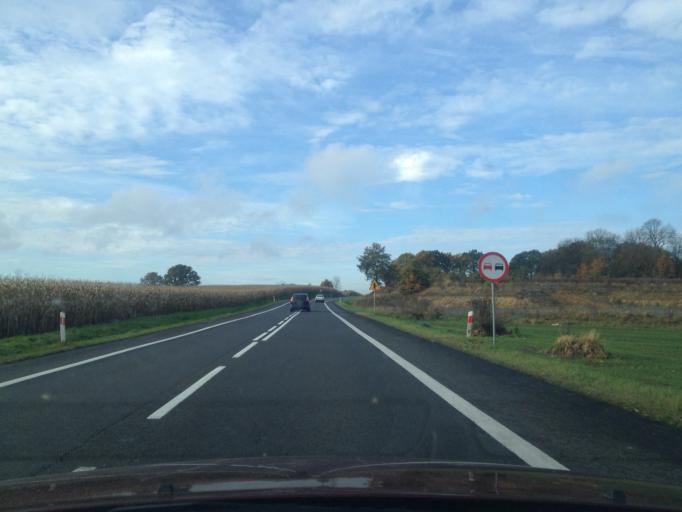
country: PL
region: Lower Silesian Voivodeship
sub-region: Powiat lubanski
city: Pisarzowice
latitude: 51.1448
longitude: 15.2091
